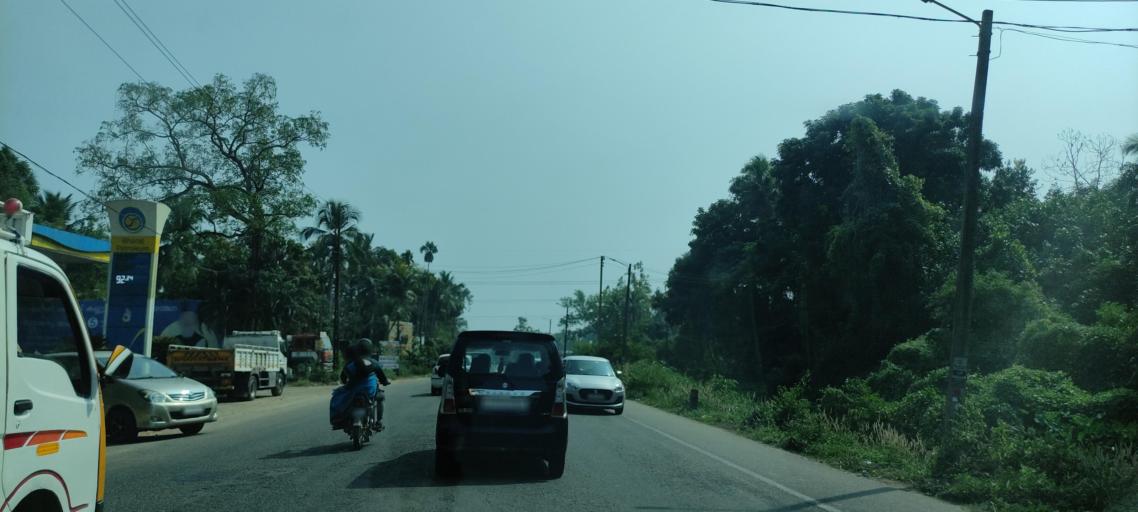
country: IN
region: Kerala
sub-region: Alappuzha
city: Kayankulam
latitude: 9.2538
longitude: 76.4655
